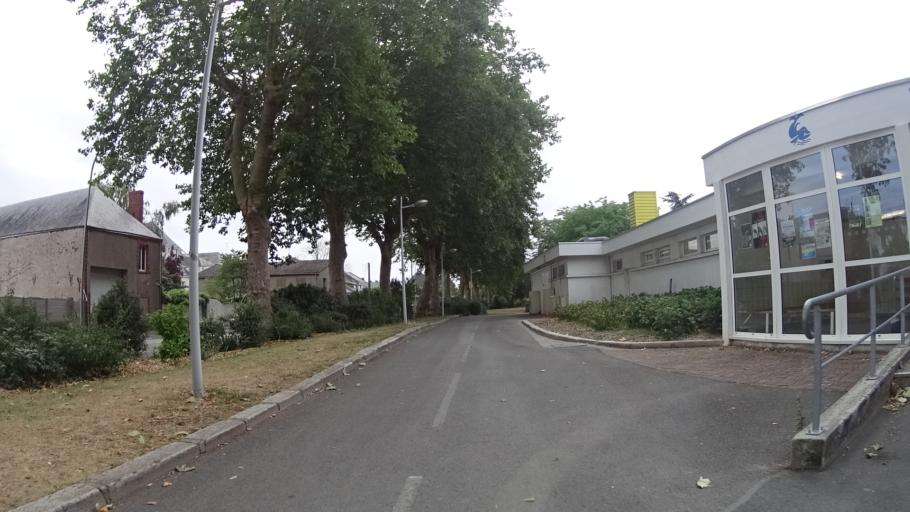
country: FR
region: Pays de la Loire
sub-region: Departement de la Loire-Atlantique
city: Ancenis
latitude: 47.3634
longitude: -1.1822
